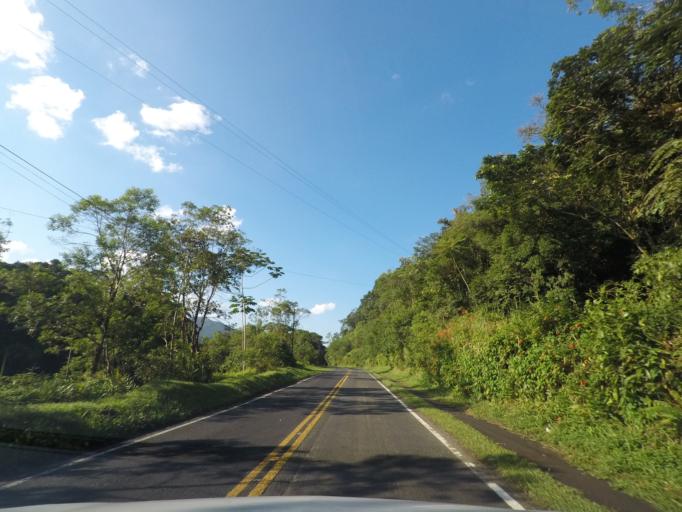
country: BR
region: Parana
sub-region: Antonina
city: Antonina
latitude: -25.3965
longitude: -48.8674
